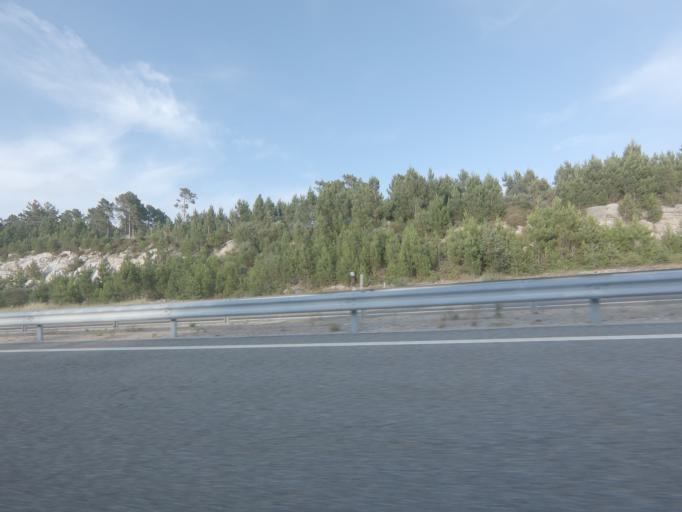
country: PT
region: Vila Real
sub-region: Vila Pouca de Aguiar
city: Vila Pouca de Aguiar
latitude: 41.5016
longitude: -7.6561
